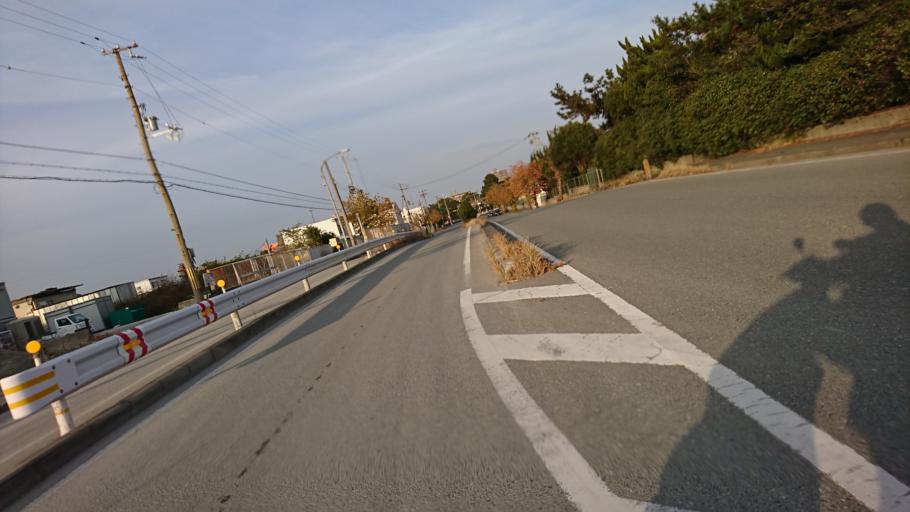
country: JP
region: Hyogo
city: Kakogawacho-honmachi
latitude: 34.7209
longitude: 134.8445
